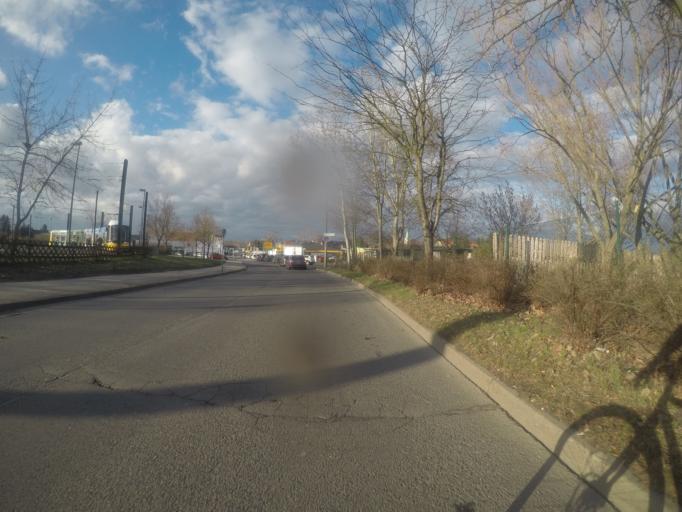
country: DE
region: Brandenburg
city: Ahrensfelde
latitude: 52.5732
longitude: 13.5752
